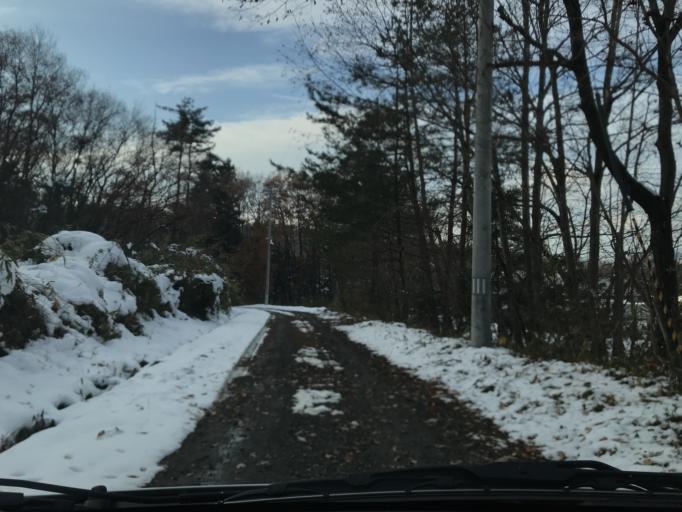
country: JP
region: Iwate
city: Mizusawa
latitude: 39.0404
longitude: 141.1030
